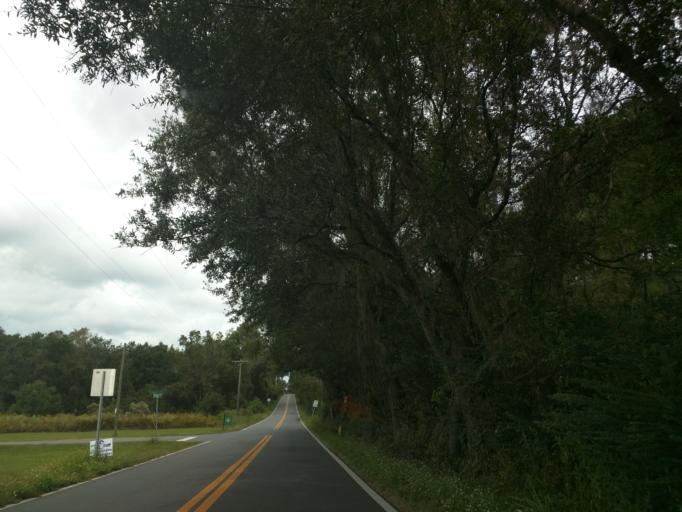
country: US
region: Florida
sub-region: Leon County
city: Tallahassee
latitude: 30.4101
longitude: -84.2101
